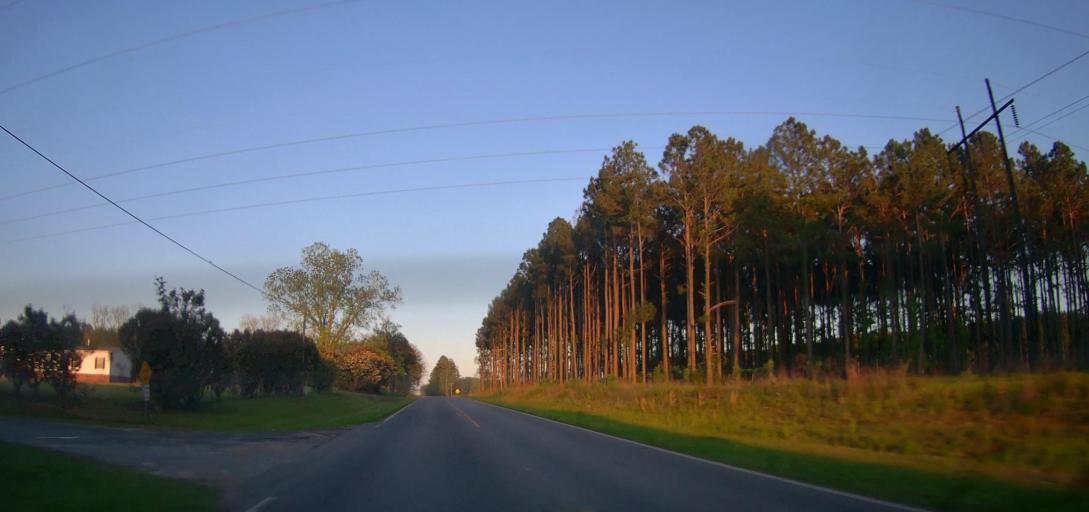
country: US
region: Georgia
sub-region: Ben Hill County
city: Fitzgerald
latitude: 31.7178
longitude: -83.2938
